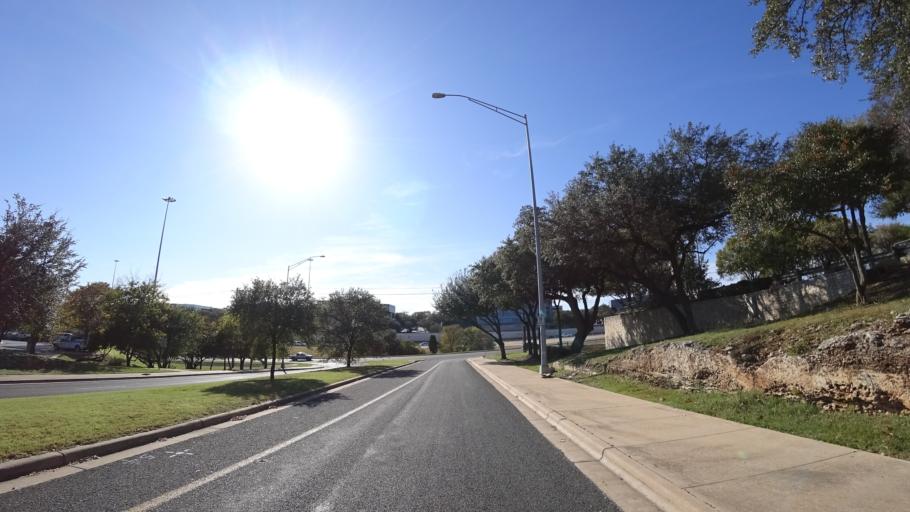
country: US
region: Texas
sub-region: Williamson County
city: Jollyville
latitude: 30.3855
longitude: -97.7413
